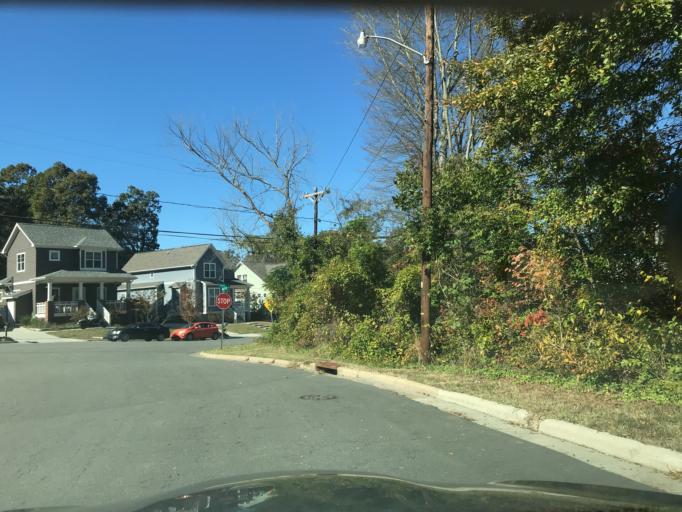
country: US
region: North Carolina
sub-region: Durham County
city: Durham
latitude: 35.9856
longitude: -78.9054
